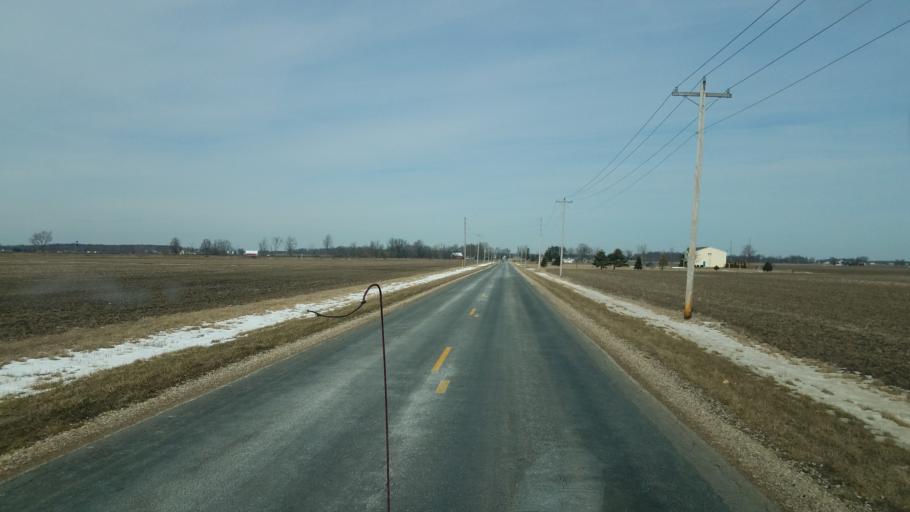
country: US
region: Ohio
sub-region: Delaware County
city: Delaware
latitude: 40.3188
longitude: -83.0097
